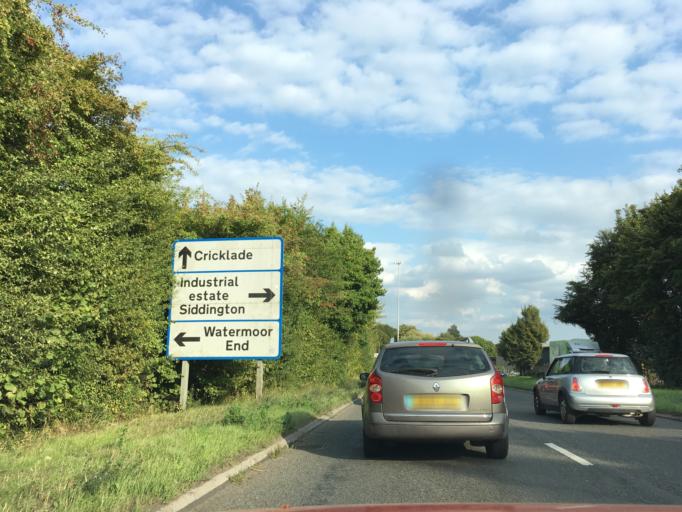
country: GB
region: England
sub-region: Gloucestershire
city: Cirencester
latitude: 51.7086
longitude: -1.9622
